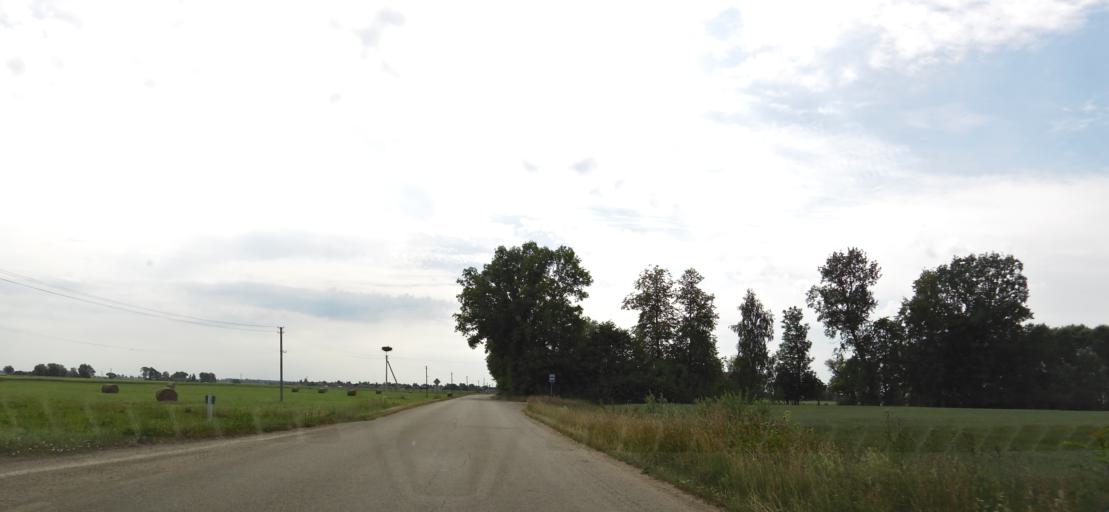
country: LT
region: Panevezys
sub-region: Birzai
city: Birzai
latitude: 56.2748
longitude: 24.5999
